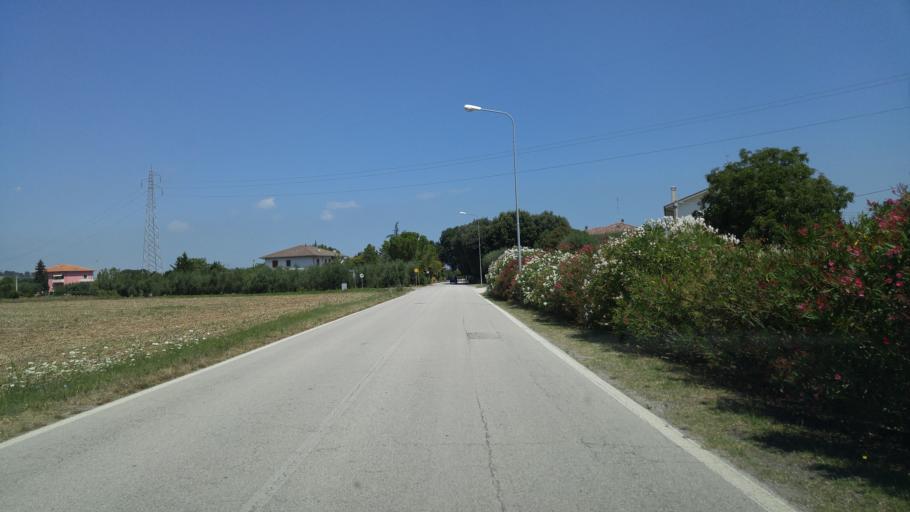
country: IT
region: The Marches
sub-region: Provincia di Pesaro e Urbino
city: Bellocchi
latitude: 43.7986
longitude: 13.0031
